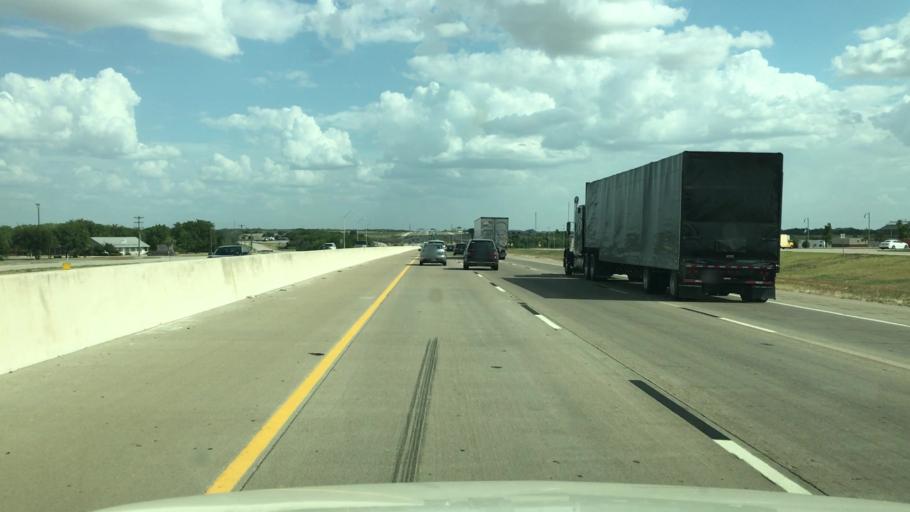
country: US
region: Texas
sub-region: Hill County
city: Hillsboro
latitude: 31.9266
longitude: -97.1022
